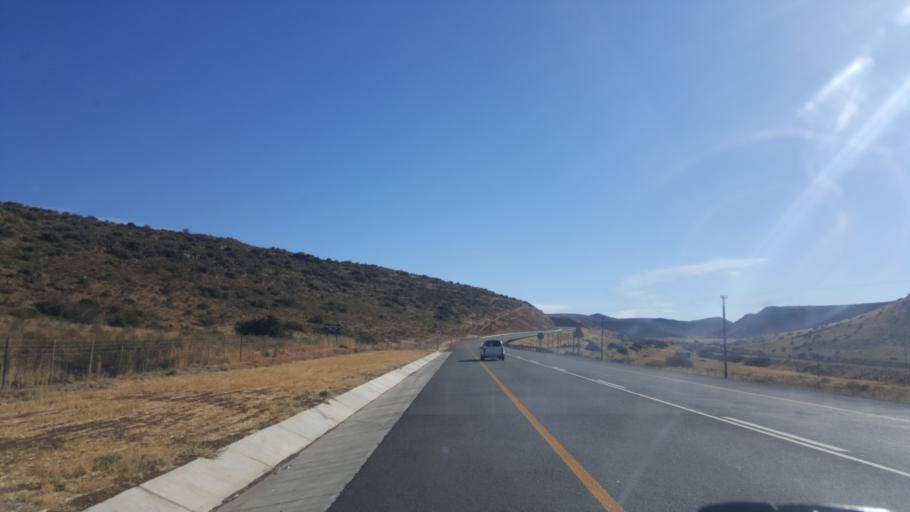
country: ZA
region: Eastern Cape
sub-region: Chris Hani District Municipality
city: Middelburg
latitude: -31.3848
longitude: 25.0318
